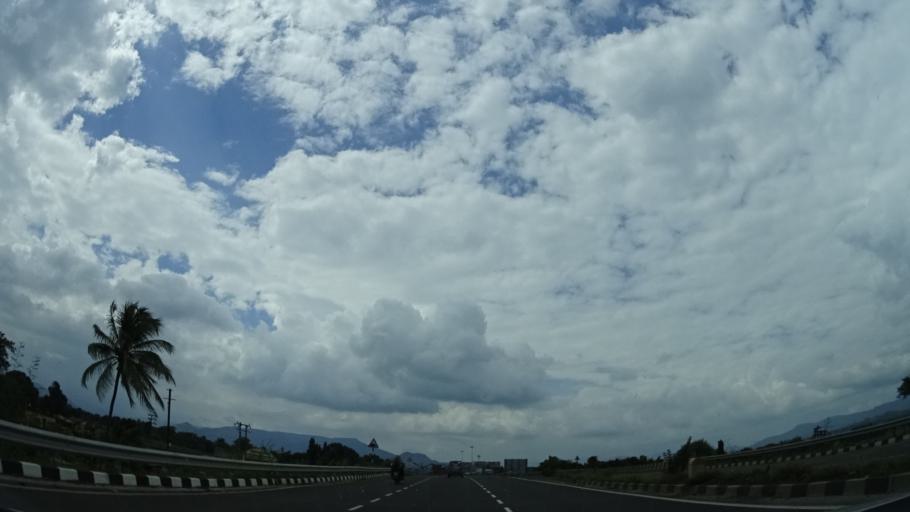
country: IN
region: Maharashtra
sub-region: Satara Division
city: Satara
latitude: 17.8054
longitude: 73.9741
